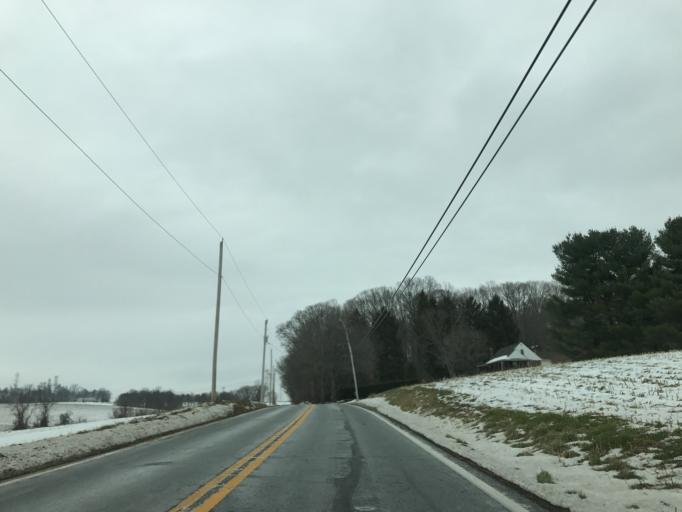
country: US
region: Pennsylvania
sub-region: York County
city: Susquehanna Trails
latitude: 39.6883
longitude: -76.4099
